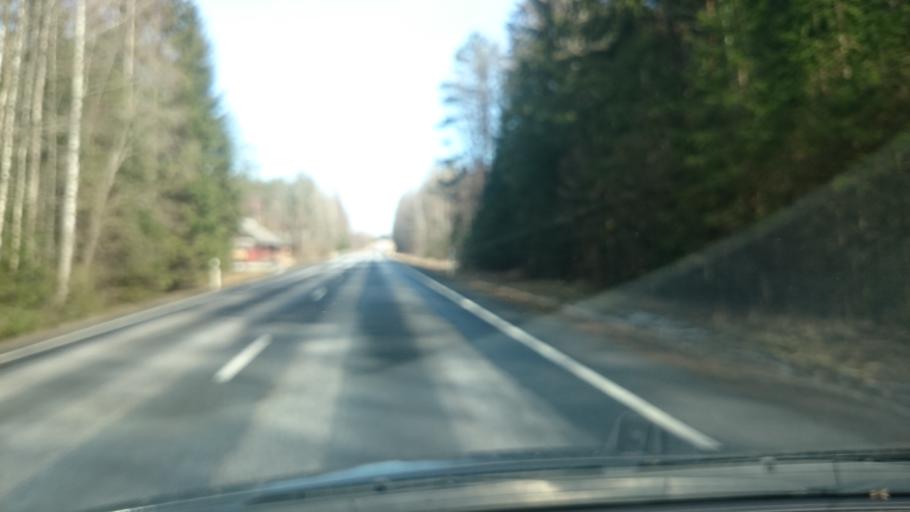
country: EE
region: Jaervamaa
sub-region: Tueri vald
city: Sarevere
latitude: 58.7433
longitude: 25.3066
